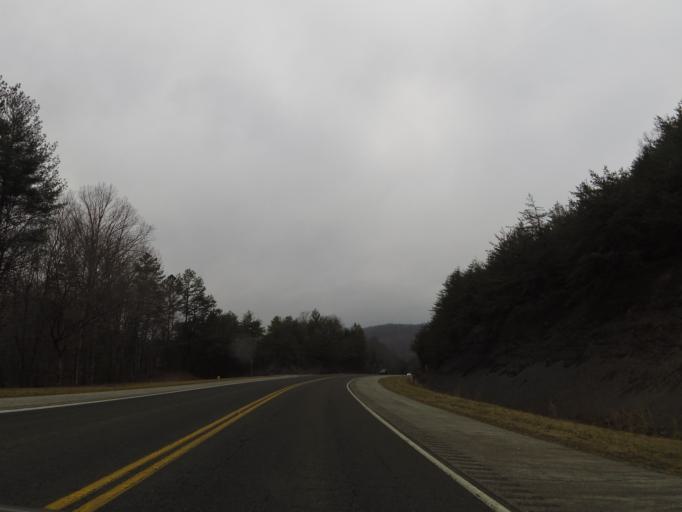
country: US
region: Tennessee
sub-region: Morgan County
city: Wartburg
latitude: 36.1224
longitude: -84.6122
